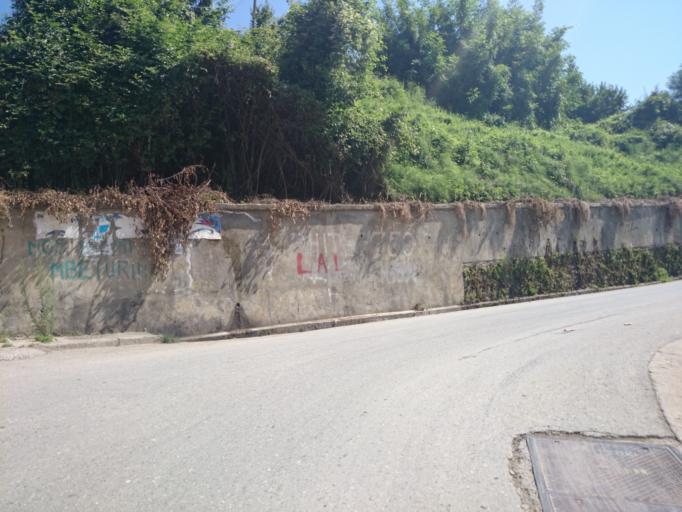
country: AL
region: Diber
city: Peshkopi
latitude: 41.6853
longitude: 20.4321
